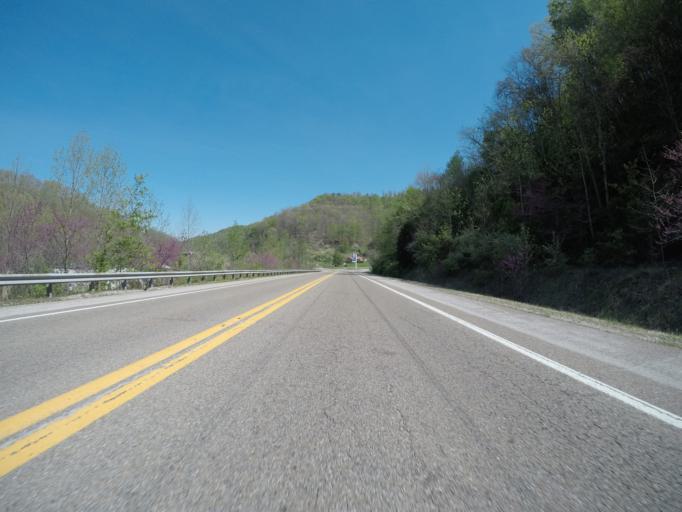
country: US
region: West Virginia
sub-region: Kanawha County
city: Charleston
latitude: 38.4127
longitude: -81.6351
